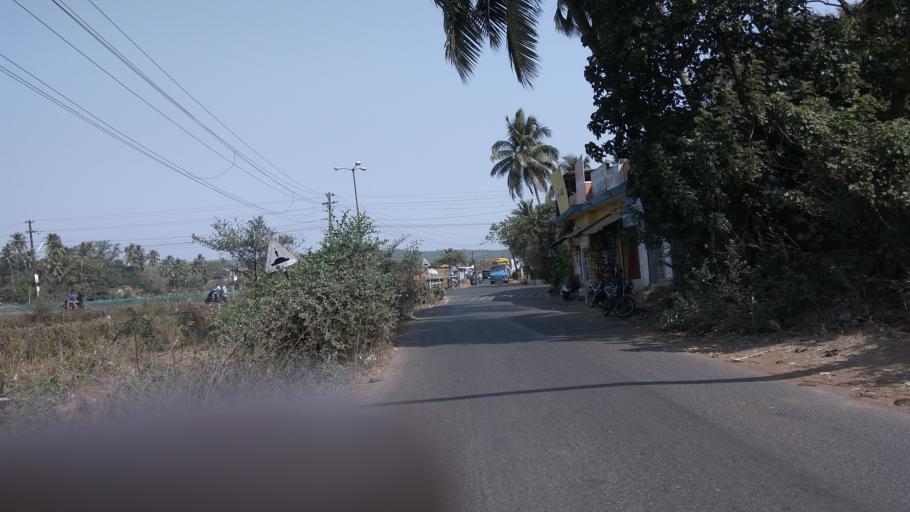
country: IN
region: Goa
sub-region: North Goa
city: Vagator
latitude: 15.5924
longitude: 73.7595
